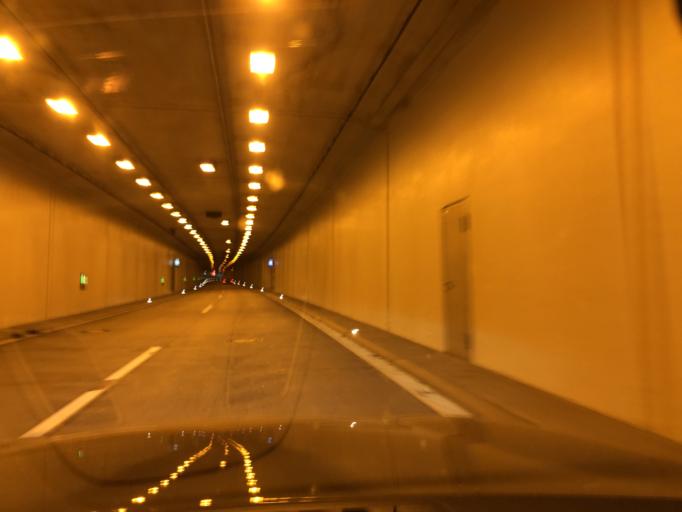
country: DE
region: Bavaria
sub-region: Swabia
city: Hopferau
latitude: 47.6040
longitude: 10.6555
